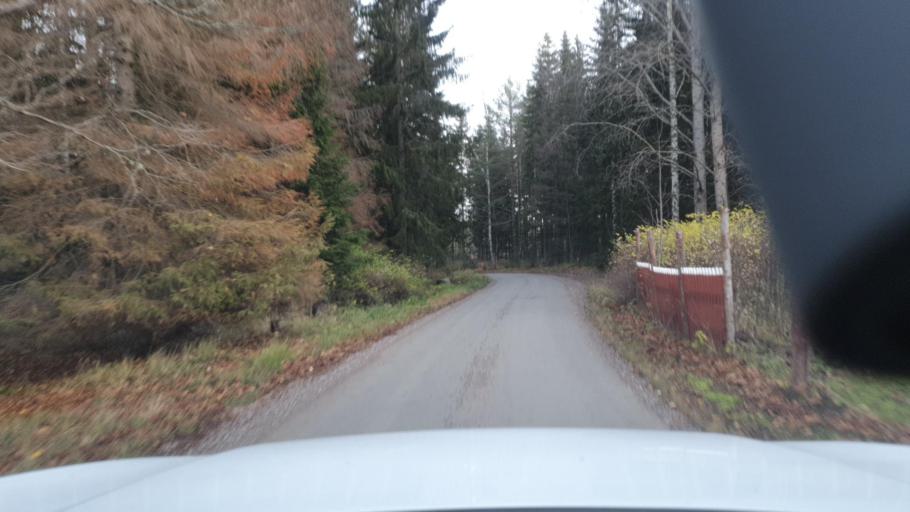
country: SE
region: Uppsala
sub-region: Alvkarleby Kommun
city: AElvkarleby
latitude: 60.4868
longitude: 17.4601
